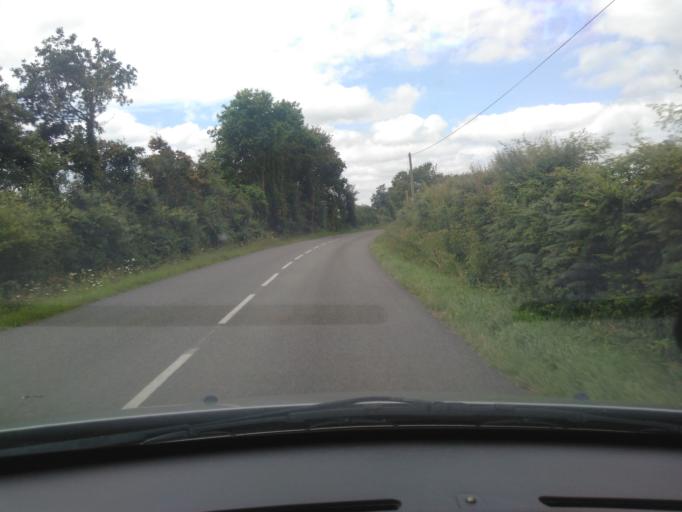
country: FR
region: Pays de la Loire
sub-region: Departement de la Vendee
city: Les Essarts
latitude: 46.7834
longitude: -1.2704
